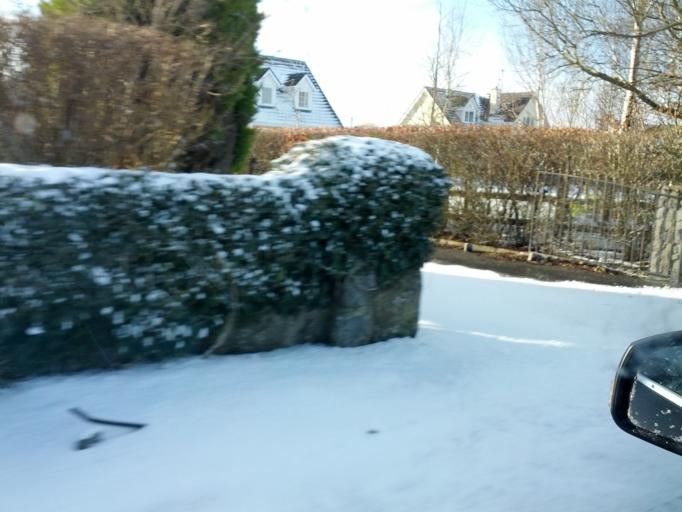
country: IE
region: Connaught
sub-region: County Galway
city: Oranmore
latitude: 53.1956
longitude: -8.8360
